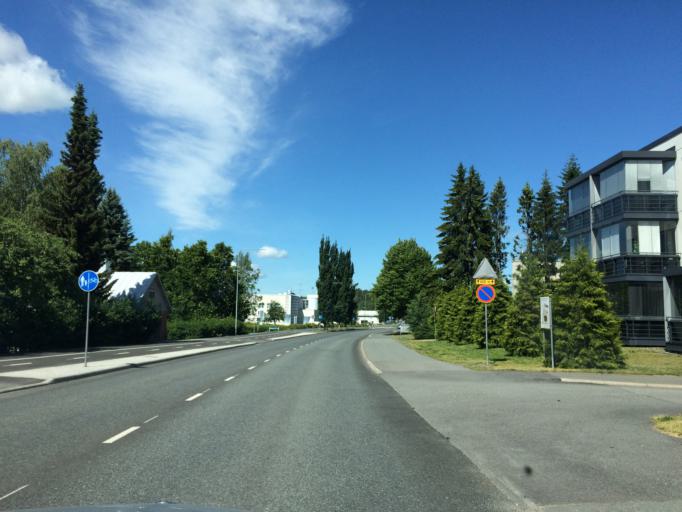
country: FI
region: Haeme
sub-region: Haemeenlinna
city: Haemeenlinna
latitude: 60.9849
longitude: 24.4427
